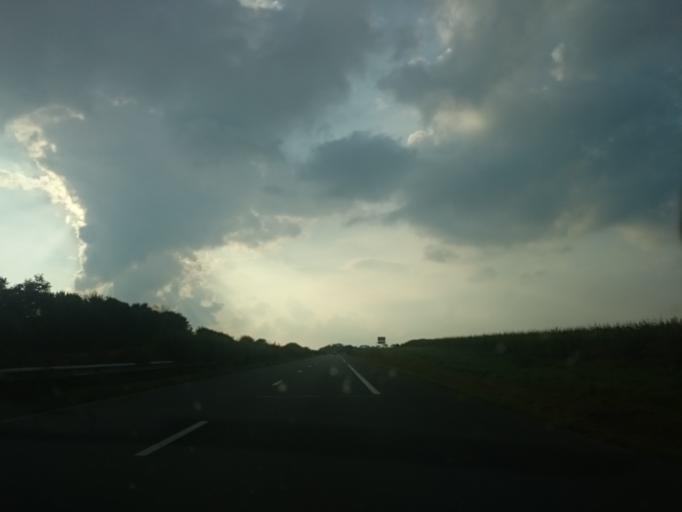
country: FR
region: Brittany
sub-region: Departement du Finistere
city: Bodilis
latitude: 48.5064
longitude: -4.1202
